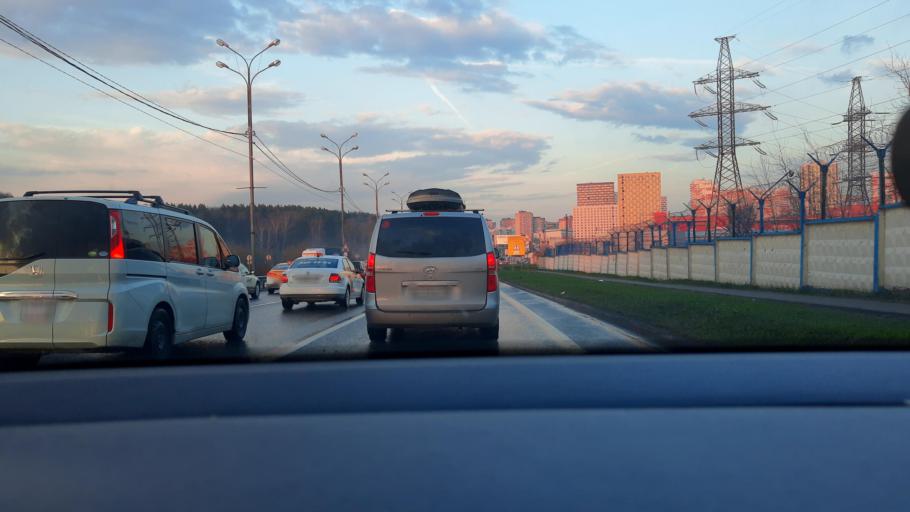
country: RU
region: Moskovskaya
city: Mytishchi
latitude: 55.9206
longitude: 37.6995
